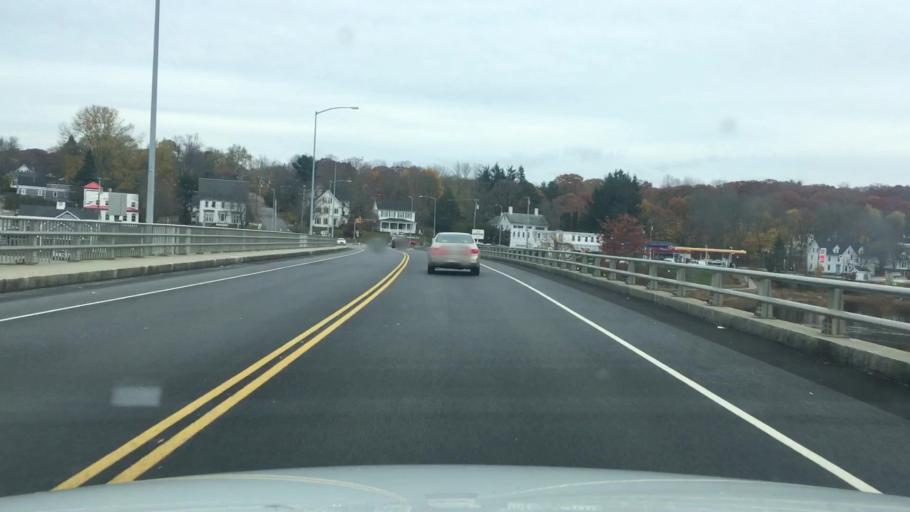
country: US
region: Maine
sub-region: Hancock County
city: Bucksport
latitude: 44.5692
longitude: -68.7883
